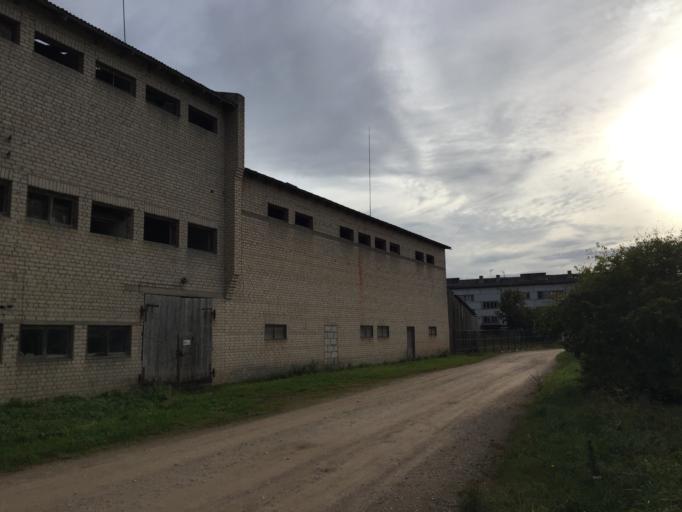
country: LV
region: Auces Novads
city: Auce
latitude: 56.5417
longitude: 22.9958
